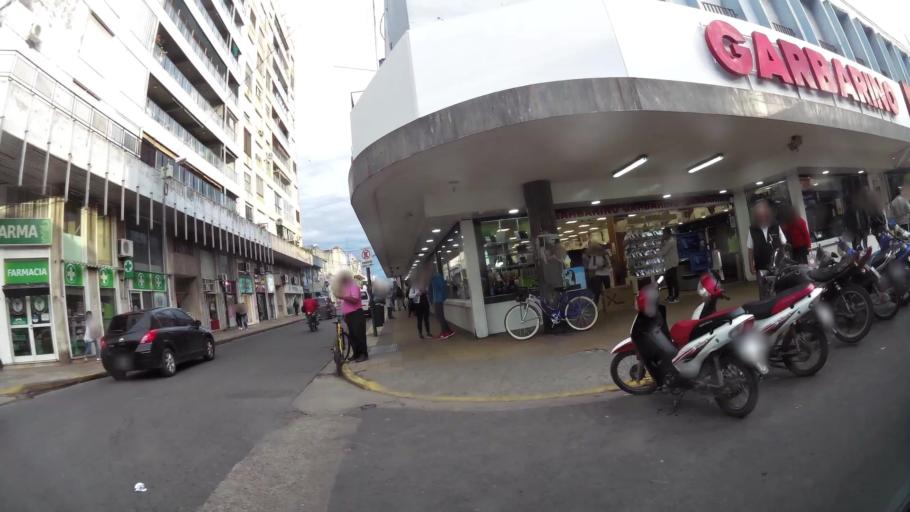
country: AR
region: Buenos Aires
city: San Nicolas de los Arroyos
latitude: -33.3305
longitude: -60.2188
